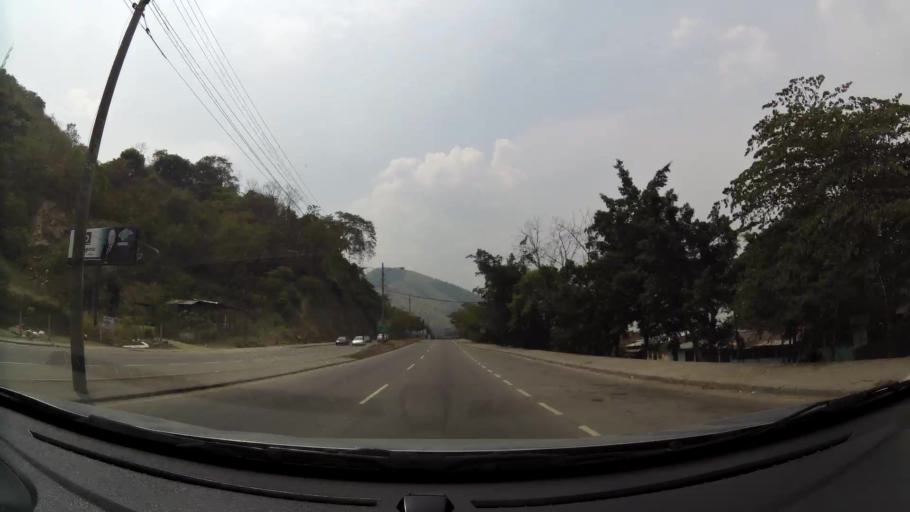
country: HN
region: Cortes
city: Chotepe
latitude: 15.4206
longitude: -88.0184
